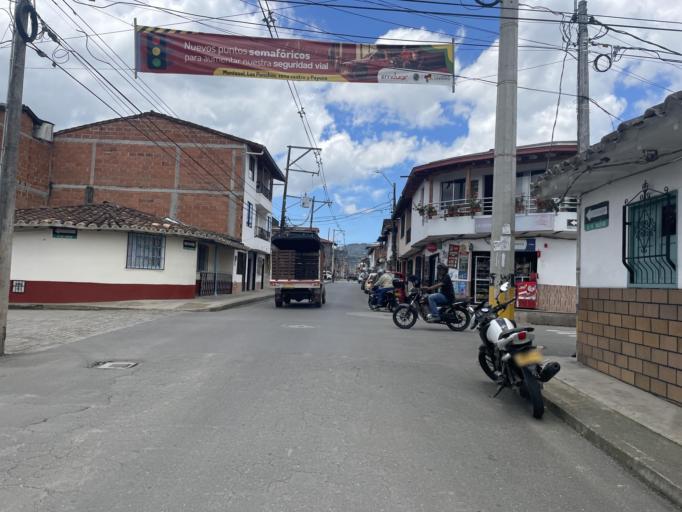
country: CO
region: Antioquia
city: La Ceja
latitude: 6.0349
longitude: -75.4291
